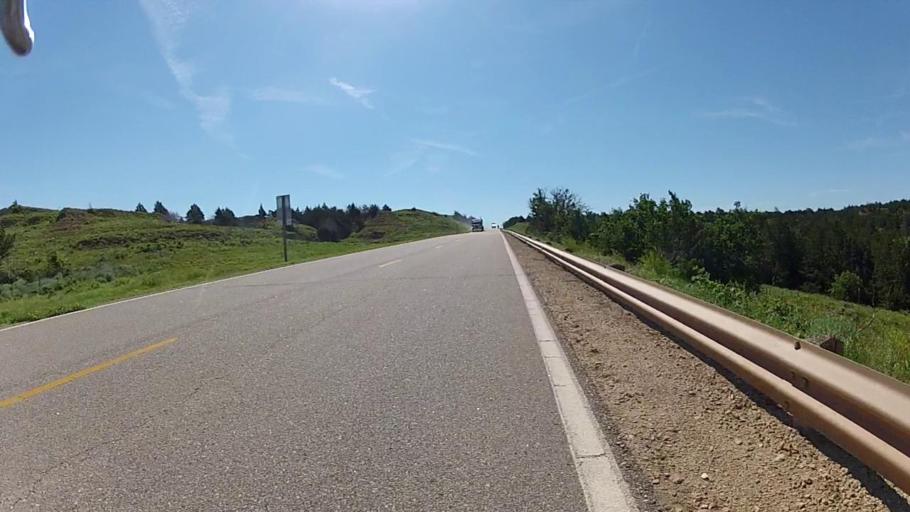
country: US
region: Kansas
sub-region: Barber County
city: Medicine Lodge
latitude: 37.2803
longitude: -98.7460
